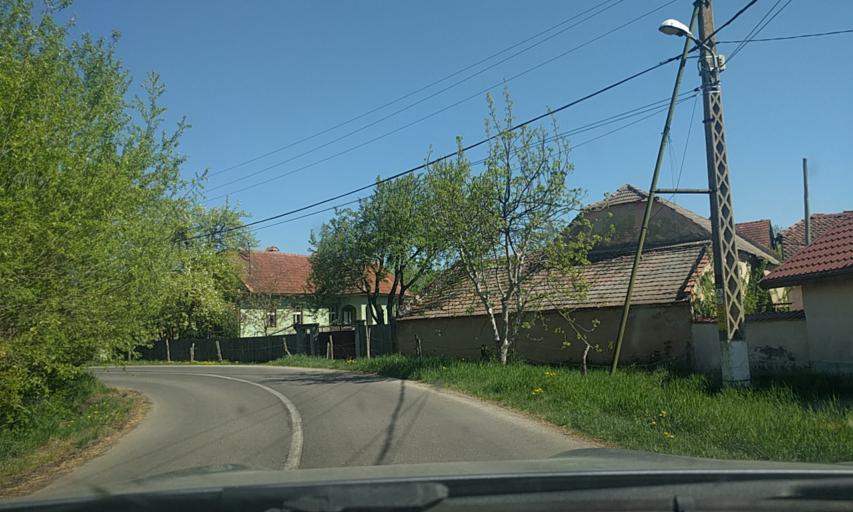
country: RO
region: Brasov
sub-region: Comuna Bod
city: Colonia Bod
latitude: 45.7096
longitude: 25.5701
